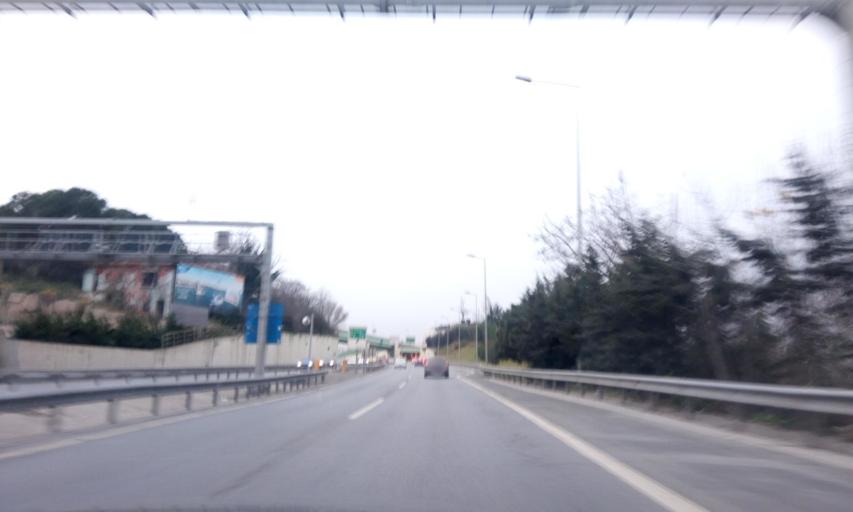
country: TR
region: Istanbul
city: UEskuedar
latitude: 41.0231
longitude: 29.0612
